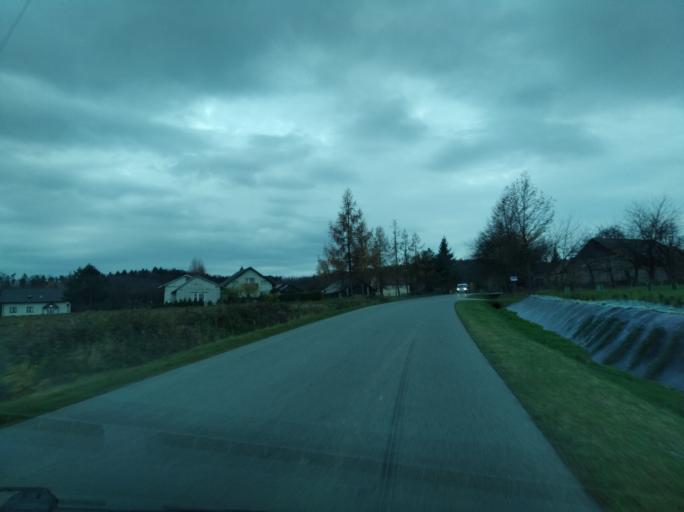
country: PL
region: Subcarpathian Voivodeship
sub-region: Powiat ropczycko-sedziszowski
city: Zagorzyce
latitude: 49.9717
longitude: 21.7026
